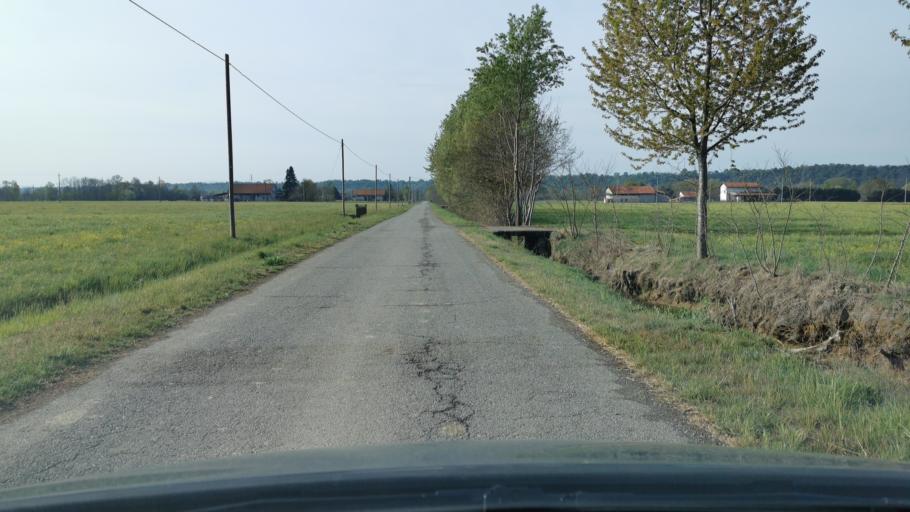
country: IT
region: Piedmont
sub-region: Provincia di Torino
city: Front
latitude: 45.2864
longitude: 7.6883
